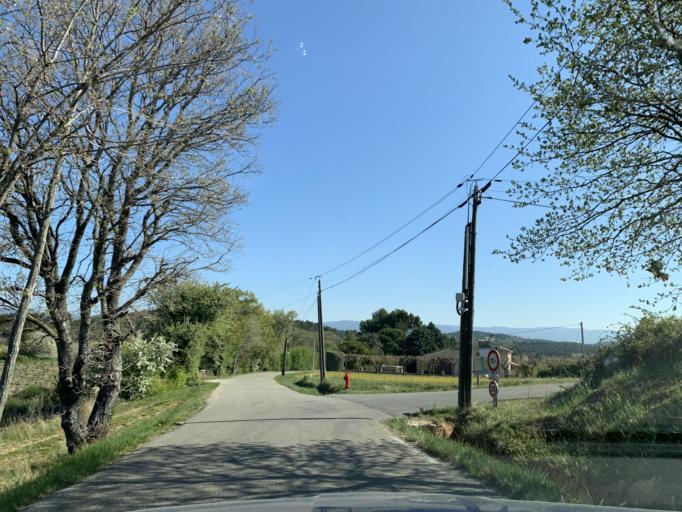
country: FR
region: Provence-Alpes-Cote d'Azur
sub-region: Departement du Vaucluse
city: Goult
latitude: 43.8812
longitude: 5.2668
